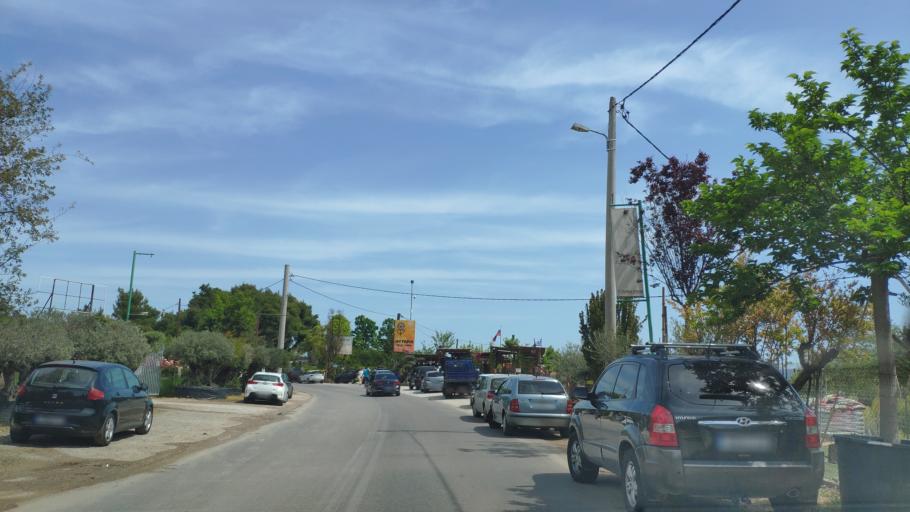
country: GR
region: Attica
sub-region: Nomarchia Anatolikis Attikis
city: Agios Stefanos
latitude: 38.1682
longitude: 23.8620
